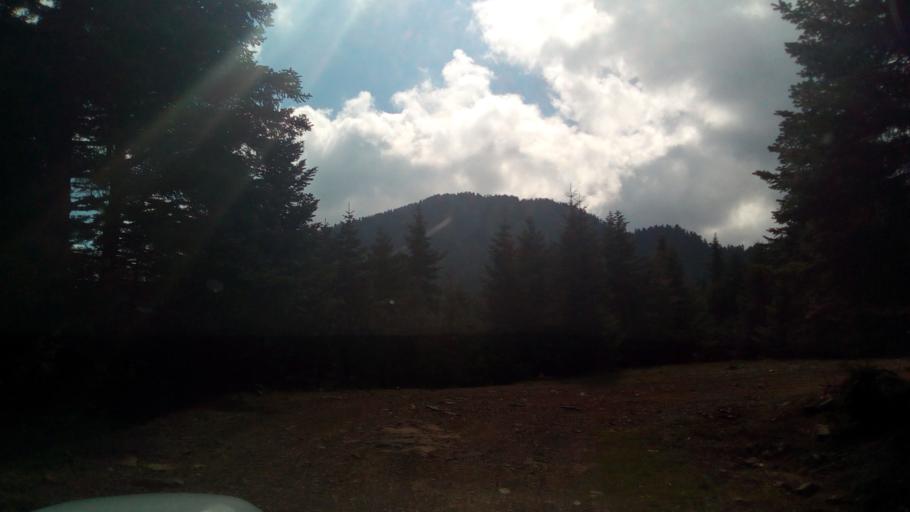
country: GR
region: Central Greece
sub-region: Nomos Fokidos
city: Lidoriki
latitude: 38.6393
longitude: 21.9500
